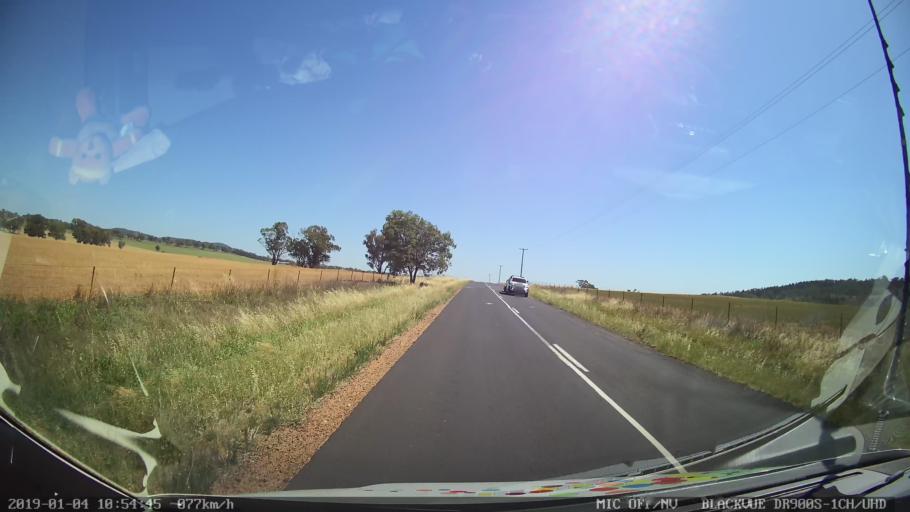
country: AU
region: New South Wales
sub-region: Cabonne
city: Molong
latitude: -33.2014
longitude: 148.6904
